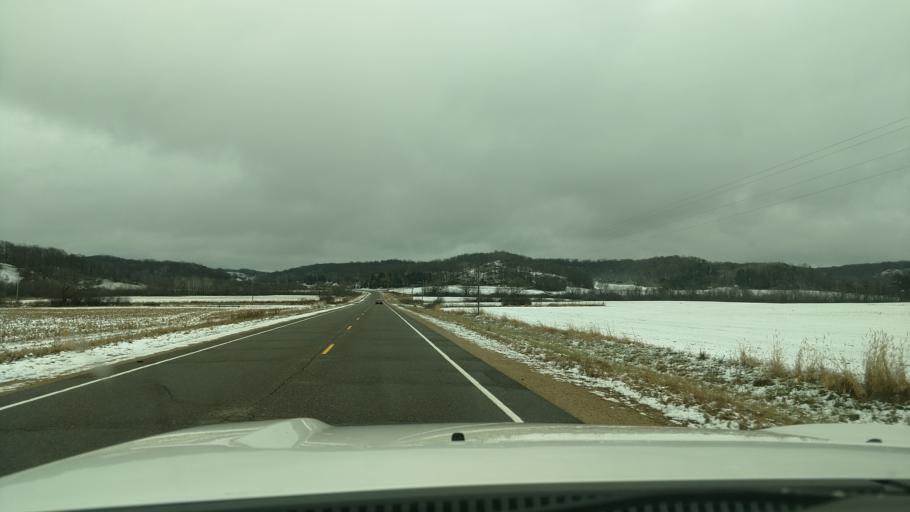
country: US
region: Wisconsin
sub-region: Dunn County
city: Tainter Lake
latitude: 45.1253
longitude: -91.8579
